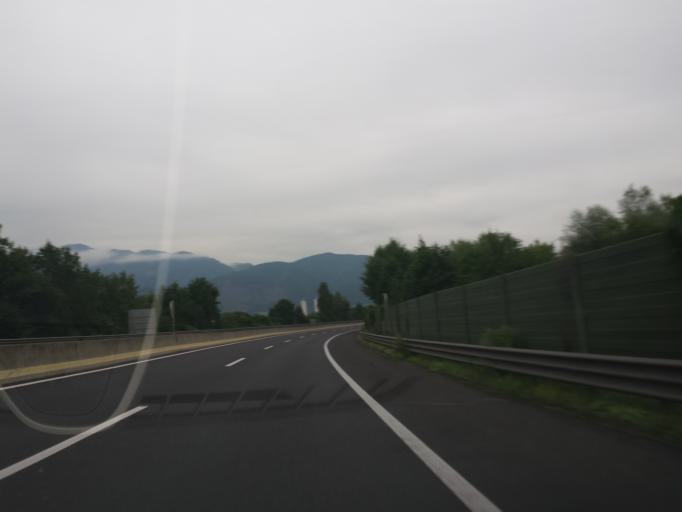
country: AT
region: Styria
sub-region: Politischer Bezirk Bruck-Muerzzuschlag
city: Sankt Marein im Muerztal
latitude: 47.4585
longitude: 15.3448
